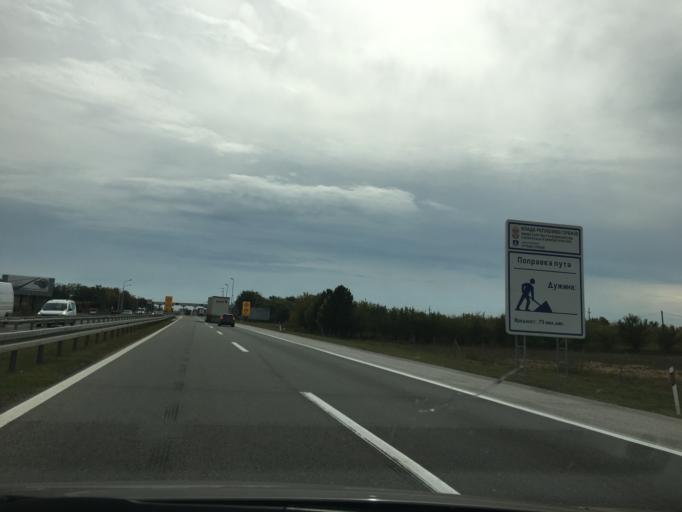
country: RS
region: Autonomna Pokrajina Vojvodina
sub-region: Sremski Okrug
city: Stara Pazova
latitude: 45.0092
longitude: 20.1998
